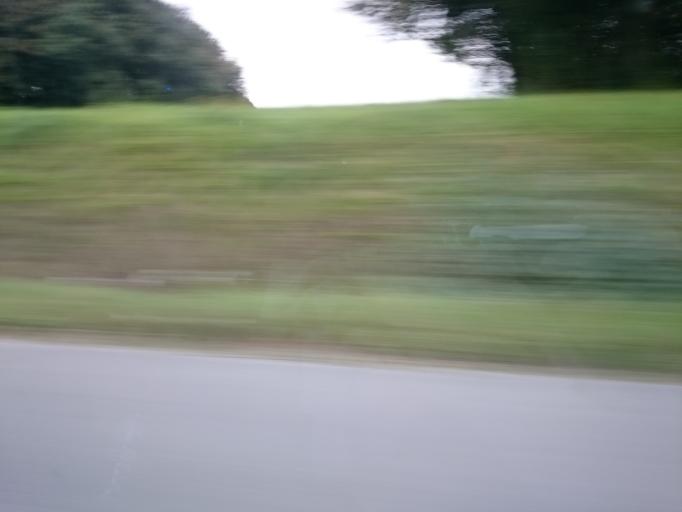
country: FR
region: Brittany
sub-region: Departement du Morbihan
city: Pluneret
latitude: 47.6605
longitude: -2.9701
